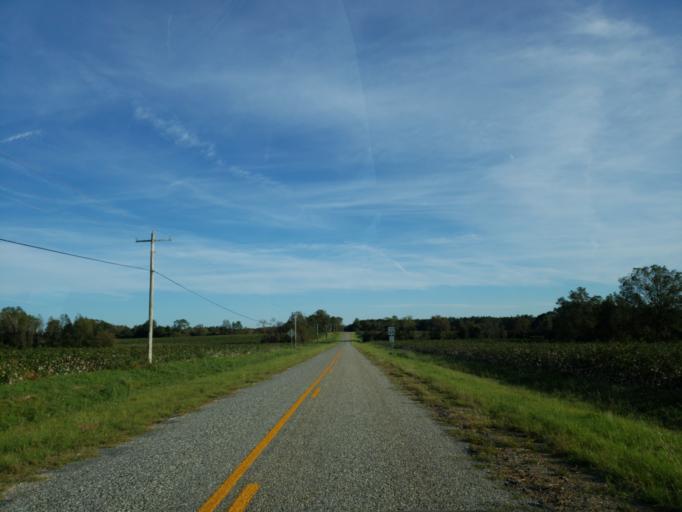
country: US
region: Georgia
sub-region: Crisp County
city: Cordele
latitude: 32.0285
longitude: -83.7437
